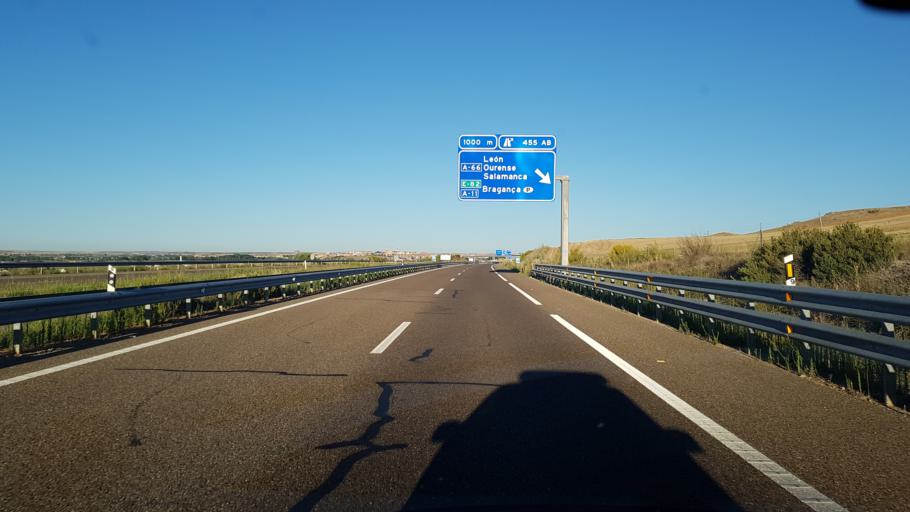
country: ES
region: Castille and Leon
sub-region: Provincia de Zamora
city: Monfarracinos
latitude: 41.5361
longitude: -5.6817
